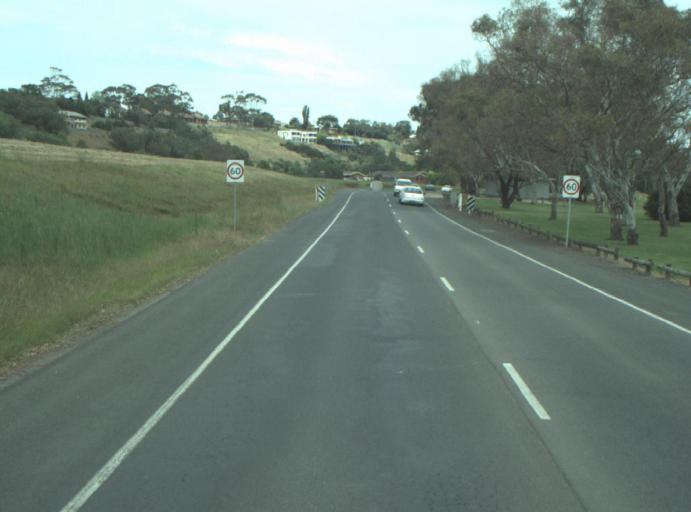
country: AU
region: Victoria
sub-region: Greater Geelong
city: Geelong
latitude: -38.1650
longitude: 144.3452
